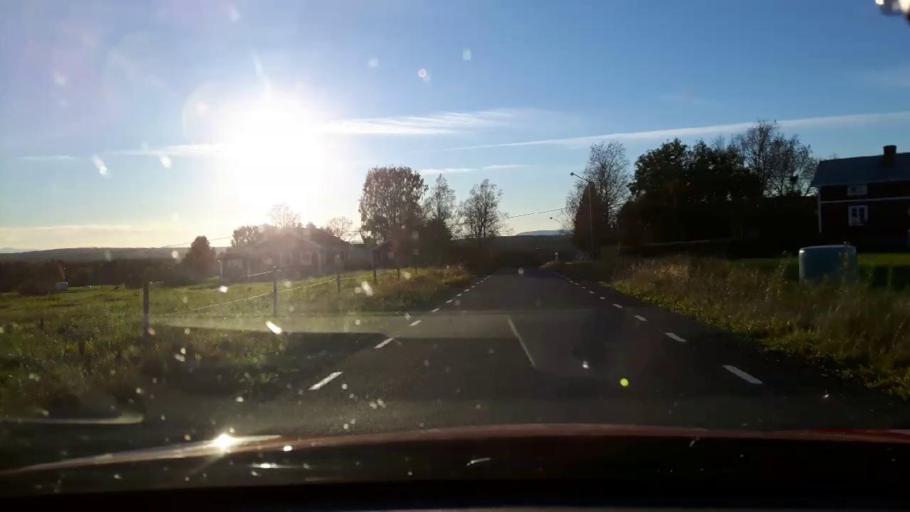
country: SE
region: Jaemtland
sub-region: OEstersunds Kommun
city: Lit
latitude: 63.4086
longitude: 14.7285
